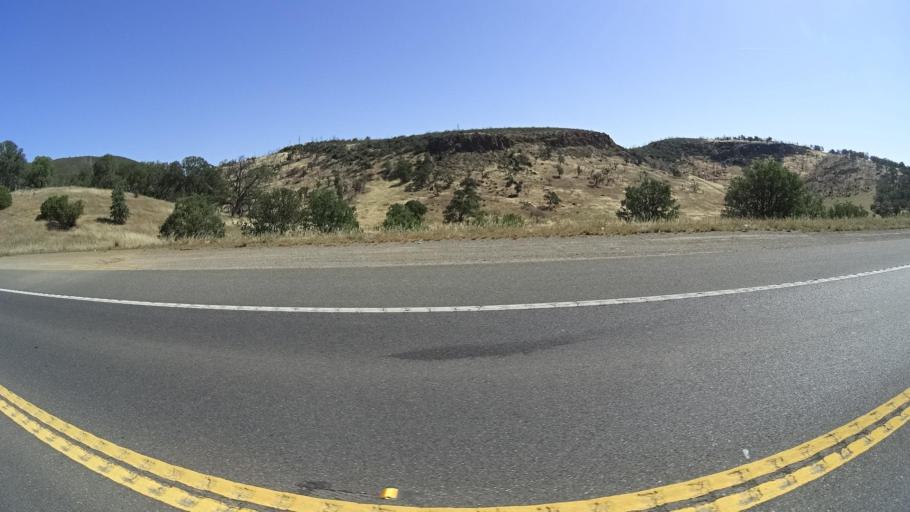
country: US
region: California
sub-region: Lake County
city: Clearlake
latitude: 39.0051
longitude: -122.6066
